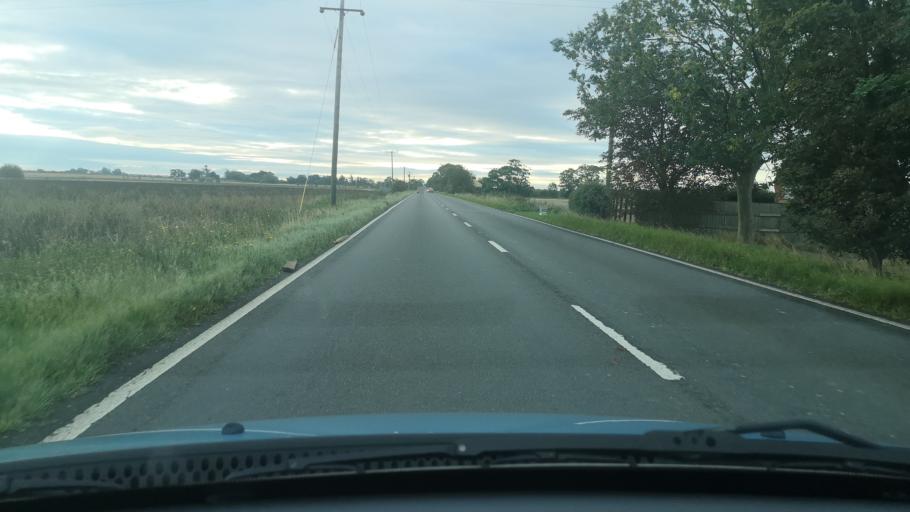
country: GB
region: England
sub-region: Doncaster
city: Hatfield
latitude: 53.5914
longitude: -0.9373
